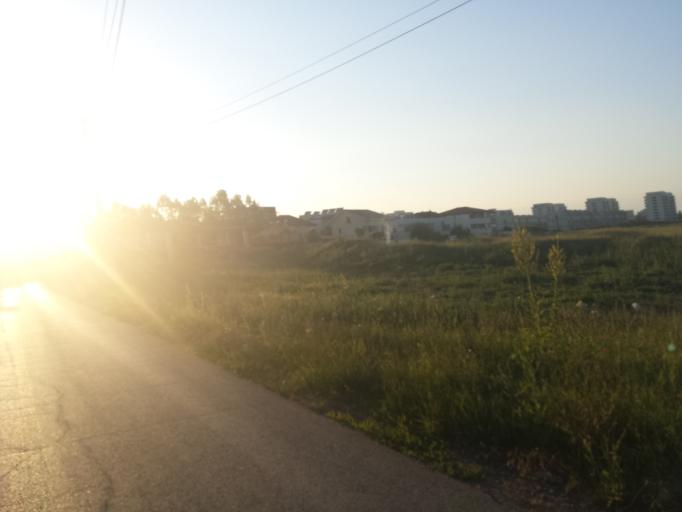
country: RO
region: Ilfov
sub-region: Comuna Tunari
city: Tunari
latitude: 44.5158
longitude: 26.1494
